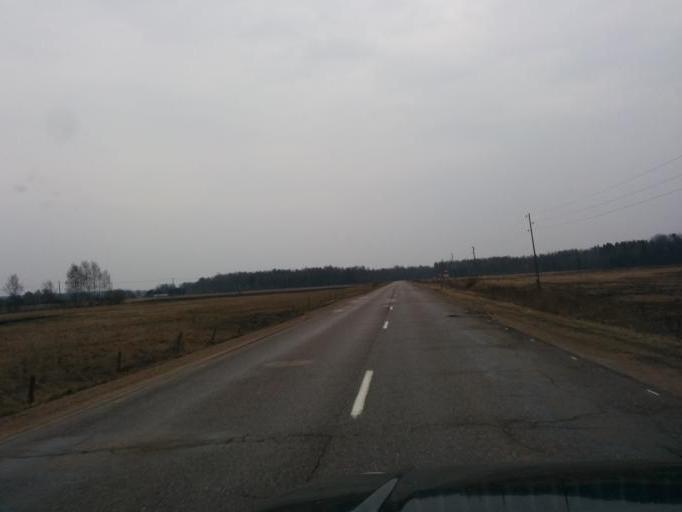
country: LV
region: Ikskile
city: Ikskile
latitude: 56.8196
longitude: 24.4535
